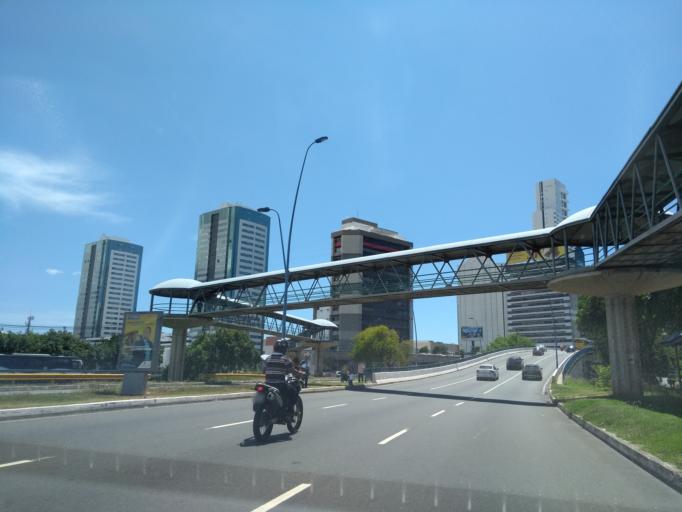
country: BR
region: Bahia
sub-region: Salvador
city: Salvador
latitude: -12.9784
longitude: -38.4602
